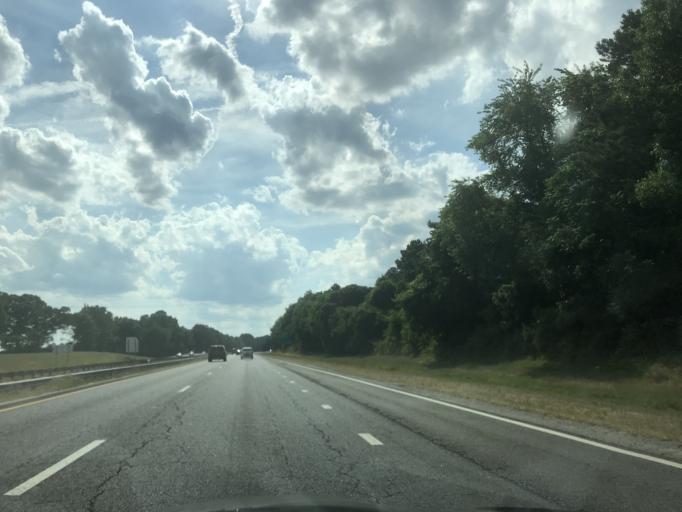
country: US
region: North Carolina
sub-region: Nash County
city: Rocky Mount
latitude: 35.9645
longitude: -77.8075
